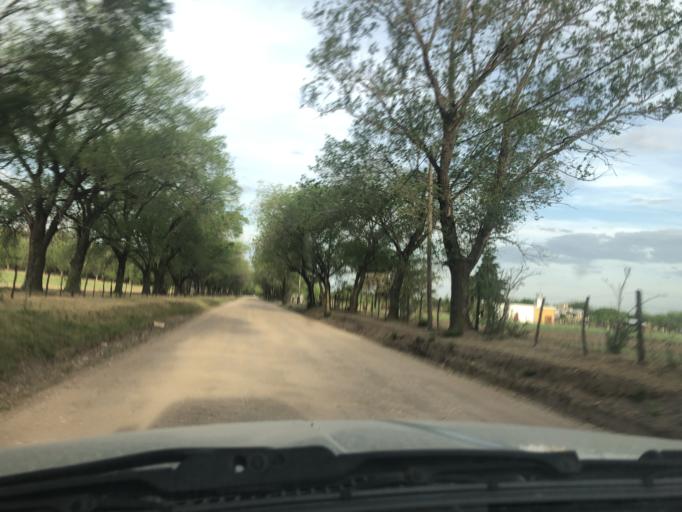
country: AR
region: Cordoba
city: La Granja
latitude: -31.0176
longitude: -64.2445
